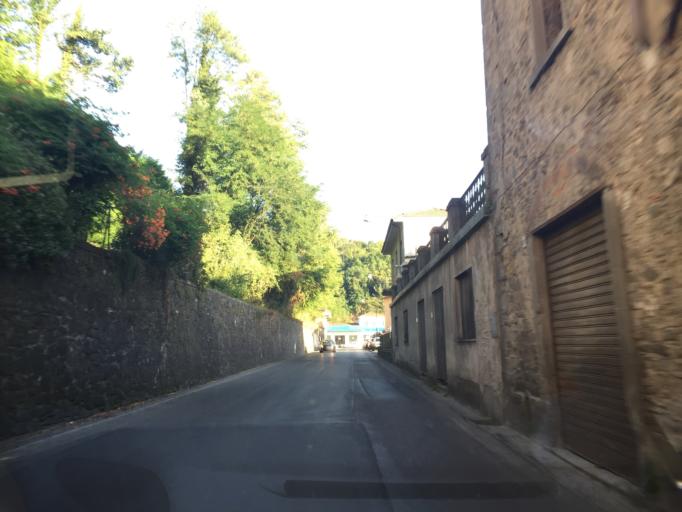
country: IT
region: Tuscany
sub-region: Provincia di Lucca
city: Castelnuovo di Garfagnana
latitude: 44.1118
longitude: 10.4131
